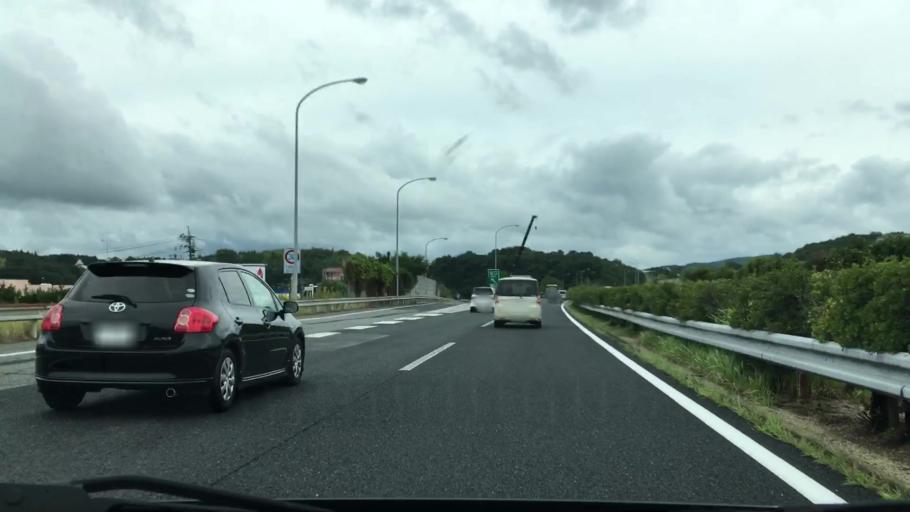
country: JP
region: Okayama
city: Tsuyama
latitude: 35.0251
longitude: 134.1650
